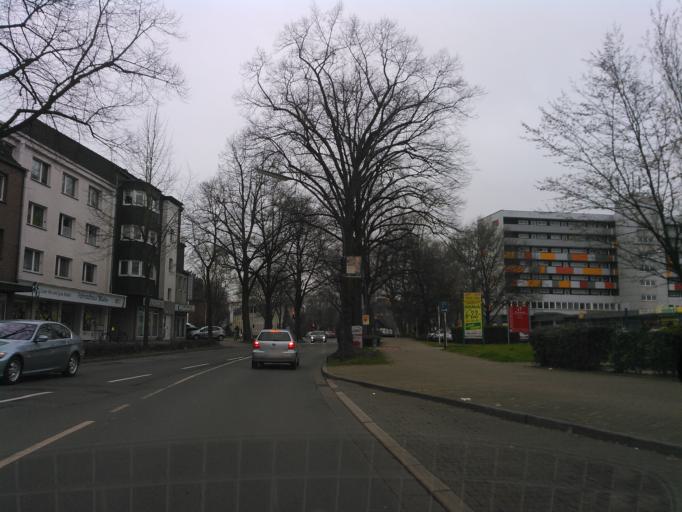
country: DE
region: North Rhine-Westphalia
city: Marl
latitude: 51.6512
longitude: 7.0883
